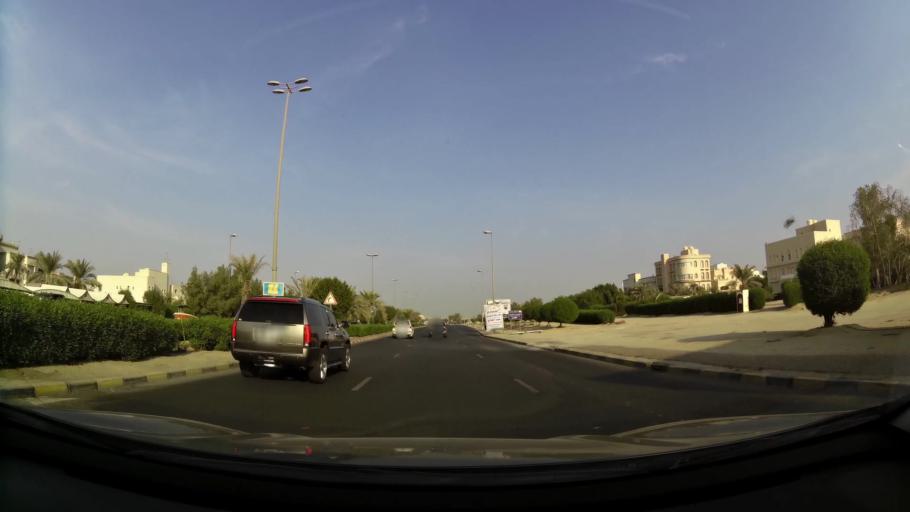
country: KW
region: Mubarak al Kabir
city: Mubarak al Kabir
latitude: 29.2074
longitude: 48.0653
